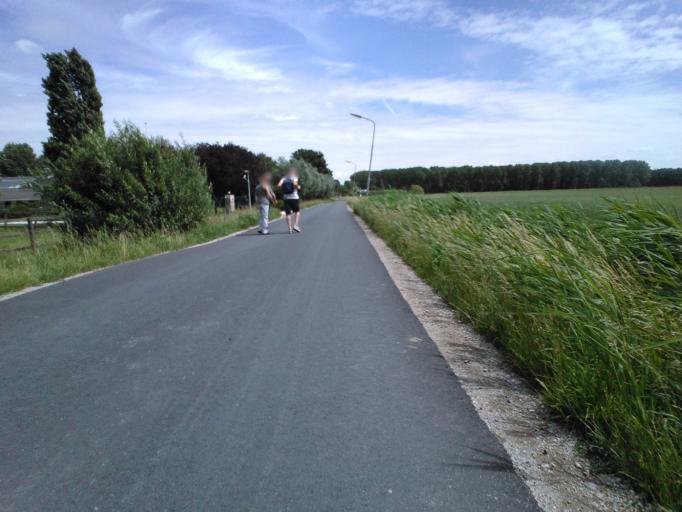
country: NL
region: South Holland
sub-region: Gemeente Alblasserdam
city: Alblasserdam
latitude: 51.8680
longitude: 4.6802
